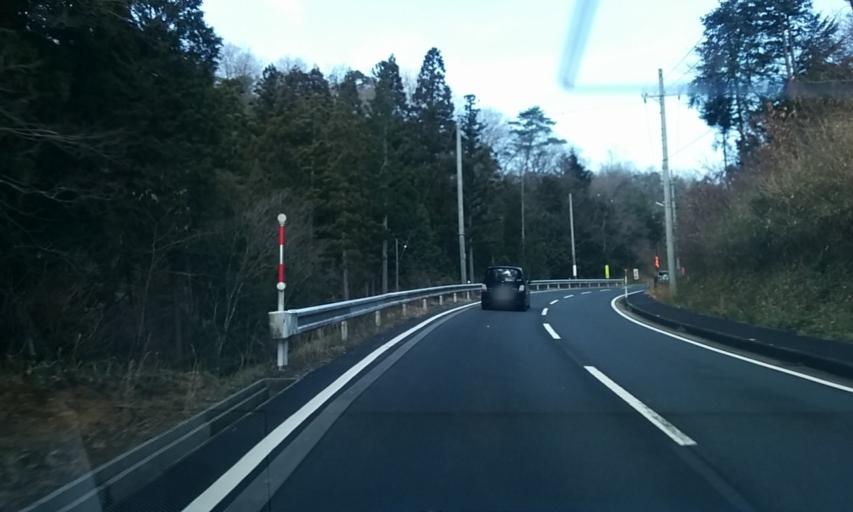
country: JP
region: Kyoto
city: Miyazu
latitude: 35.5800
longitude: 135.1187
